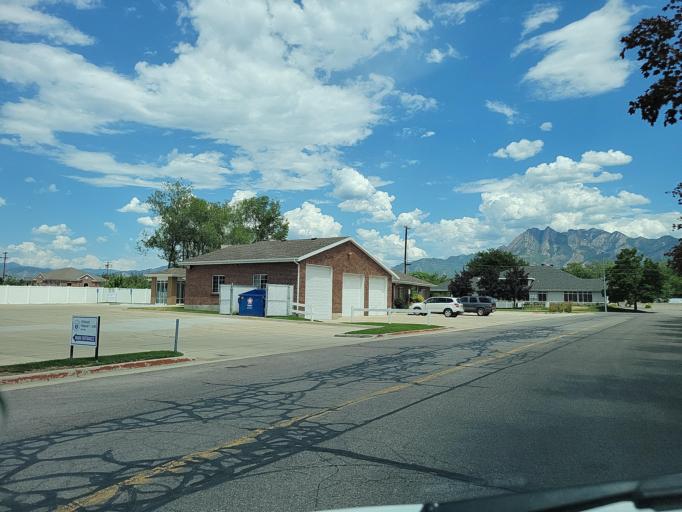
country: US
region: Utah
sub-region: Salt Lake County
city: Murray
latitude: 40.6404
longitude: -111.8840
